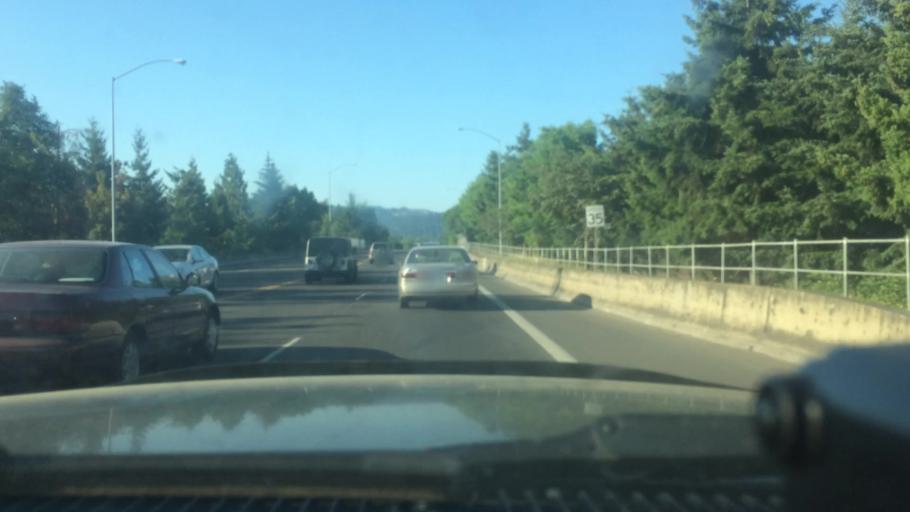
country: US
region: Oregon
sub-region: Lane County
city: Eugene
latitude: 44.0616
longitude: -123.1175
